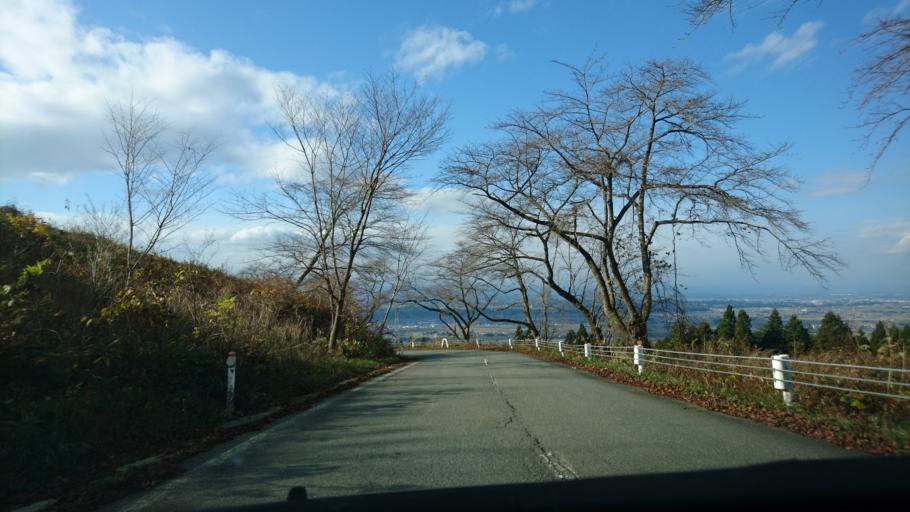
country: JP
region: Iwate
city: Ichinoseki
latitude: 39.0248
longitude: 141.1794
